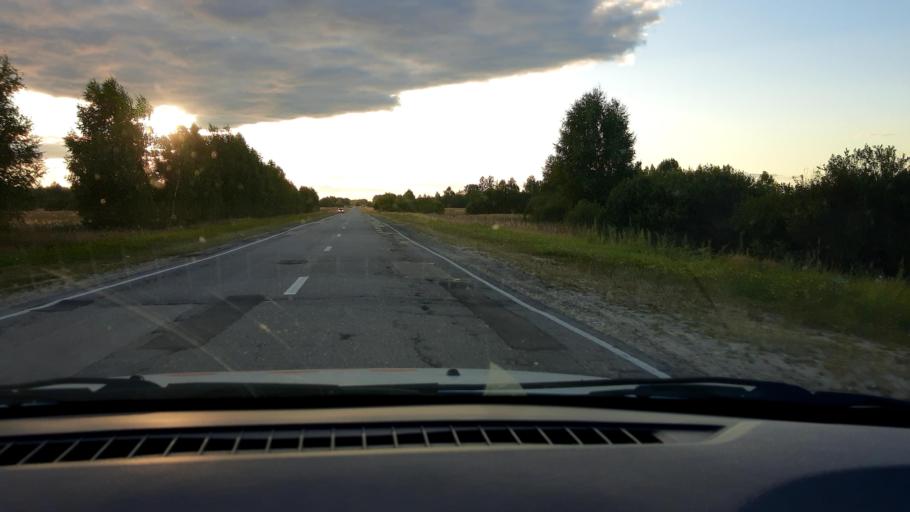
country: RU
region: Nizjnij Novgorod
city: Neklyudovo
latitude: 56.5019
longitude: 43.9866
